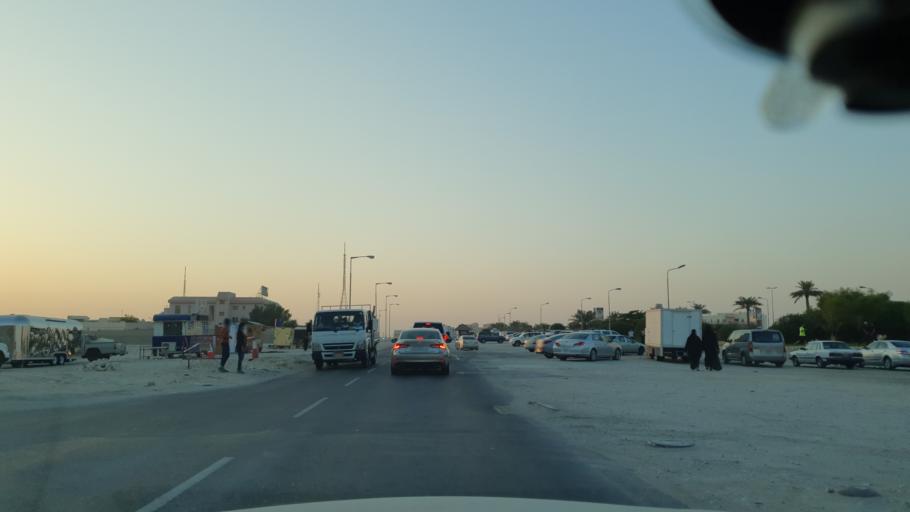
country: BH
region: Northern
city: Madinat `Isa
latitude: 26.1567
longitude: 50.5664
